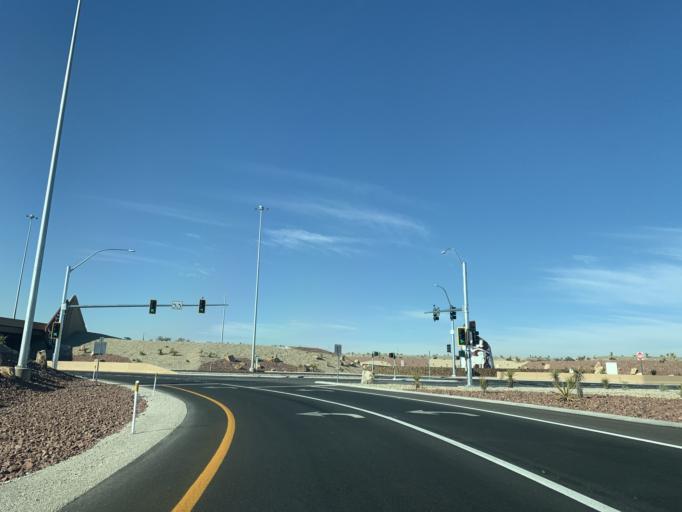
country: US
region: Nevada
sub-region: Clark County
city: Summerlin South
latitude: 36.3260
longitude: -115.3100
